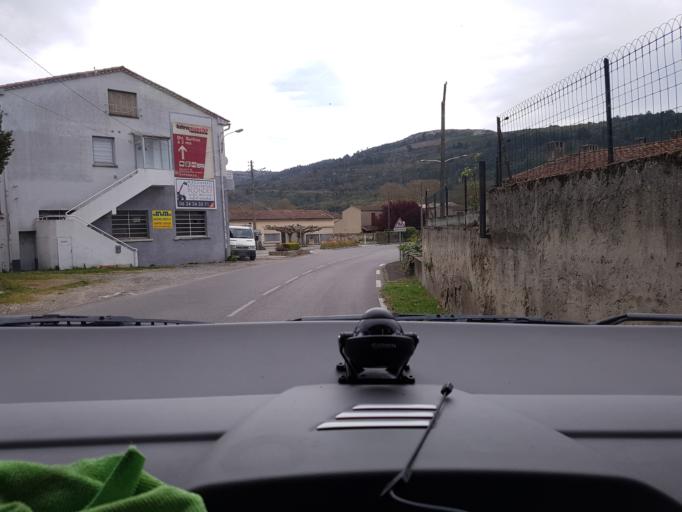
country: FR
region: Languedoc-Roussillon
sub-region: Departement de l'Aude
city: Couiza
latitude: 42.9447
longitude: 2.2561
